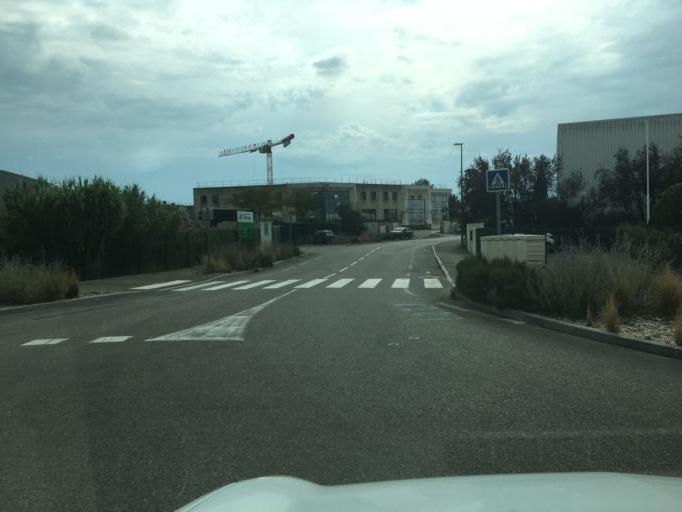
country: FR
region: Provence-Alpes-Cote d'Azur
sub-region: Departement des Bouches-du-Rhone
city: Bouc-Bel-Air
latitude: 43.4833
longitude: 5.3872
